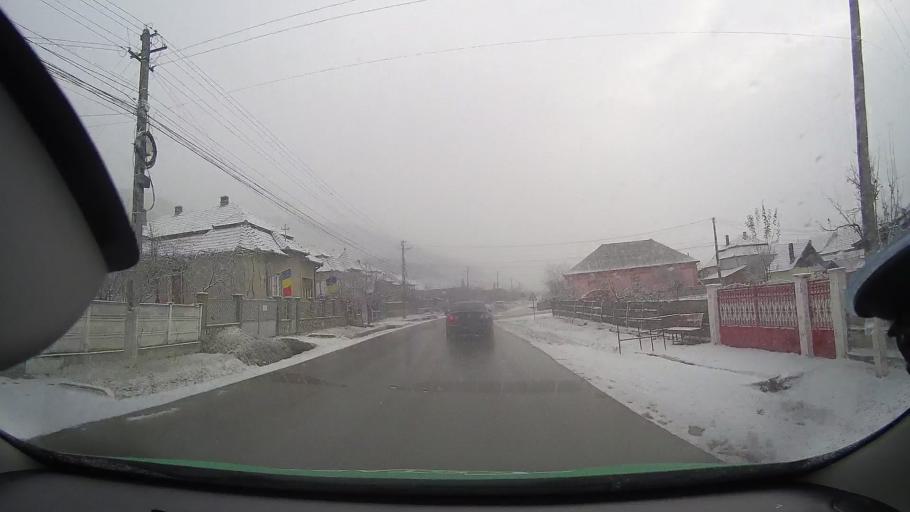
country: RO
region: Alba
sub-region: Comuna Lopadea Noua
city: Lopadea Noua
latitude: 46.3077
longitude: 23.7957
